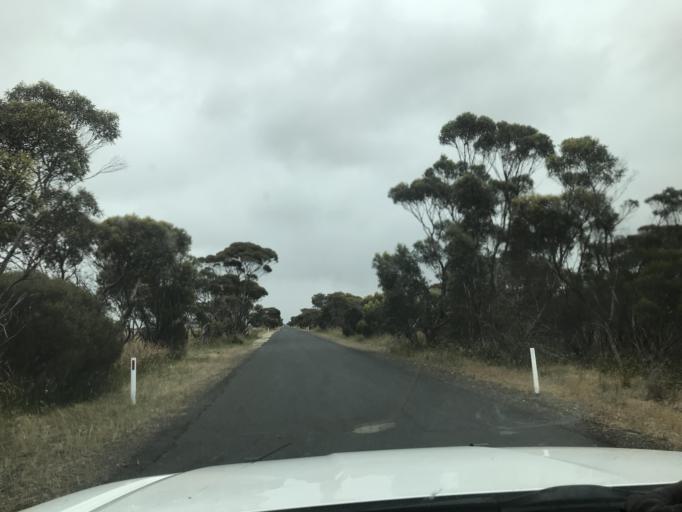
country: AU
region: South Australia
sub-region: Tatiara
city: Bordertown
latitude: -36.1189
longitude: 141.0509
